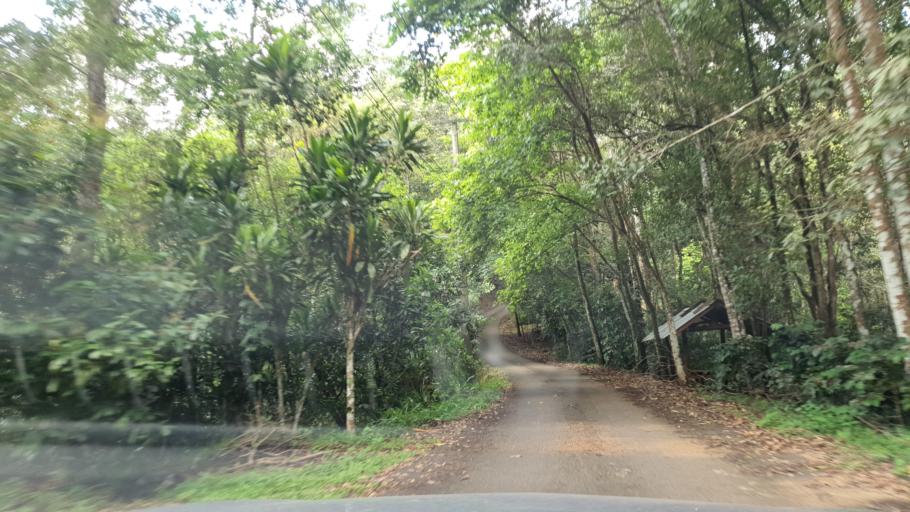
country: TH
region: Chiang Mai
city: Mae On
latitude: 18.9487
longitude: 99.3056
